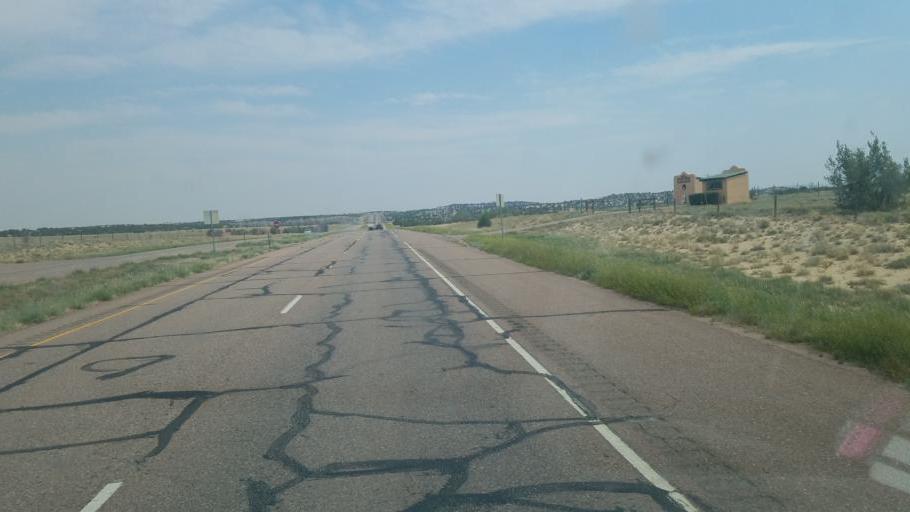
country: US
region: Colorado
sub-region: Fremont County
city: Penrose
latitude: 38.3860
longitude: -104.9610
